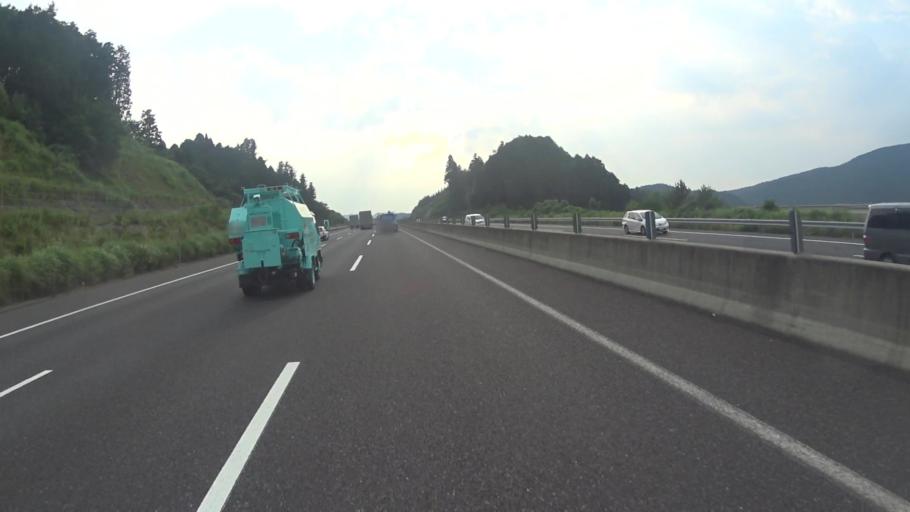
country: JP
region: Shiga Prefecture
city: Hino
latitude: 34.9165
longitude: 136.3284
